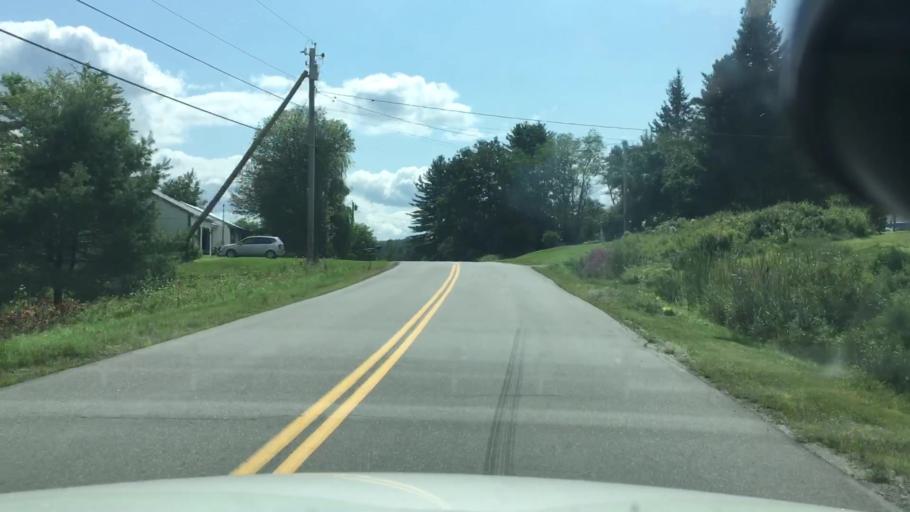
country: US
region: Maine
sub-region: Somerset County
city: Skowhegan
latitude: 44.7514
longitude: -69.7167
